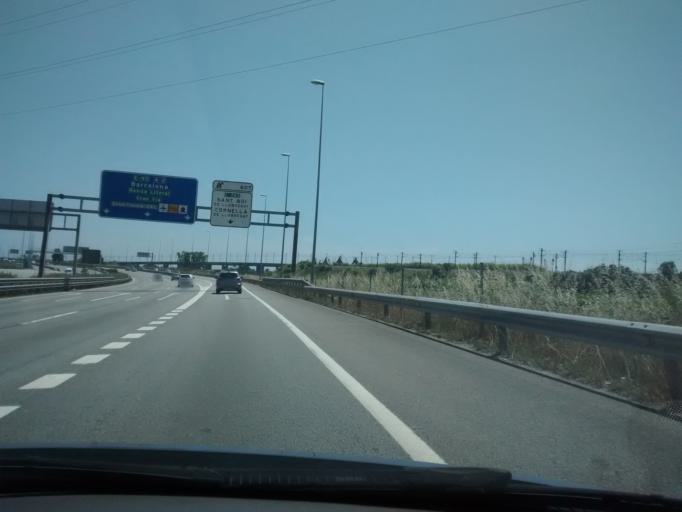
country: ES
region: Catalonia
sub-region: Provincia de Barcelona
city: Sant Joan Despi
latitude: 41.3571
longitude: 2.0515
